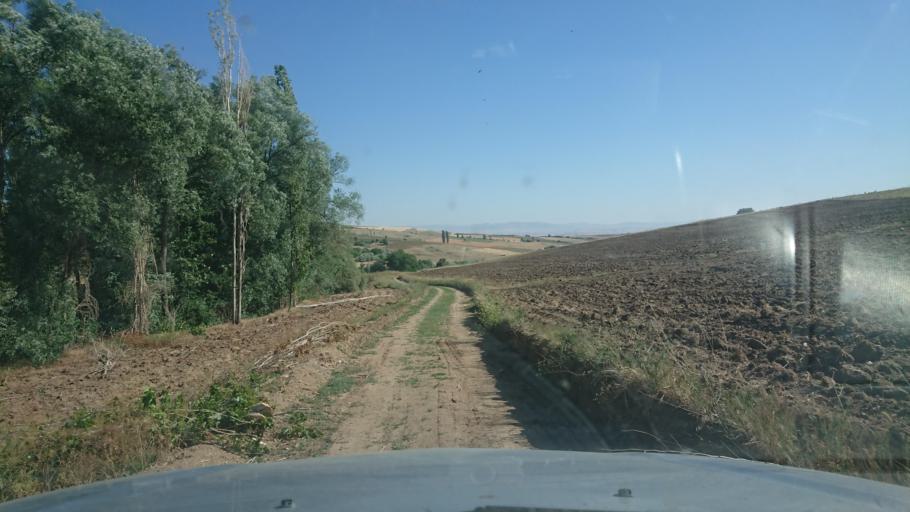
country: TR
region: Aksaray
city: Agacoren
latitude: 38.8400
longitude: 33.9257
